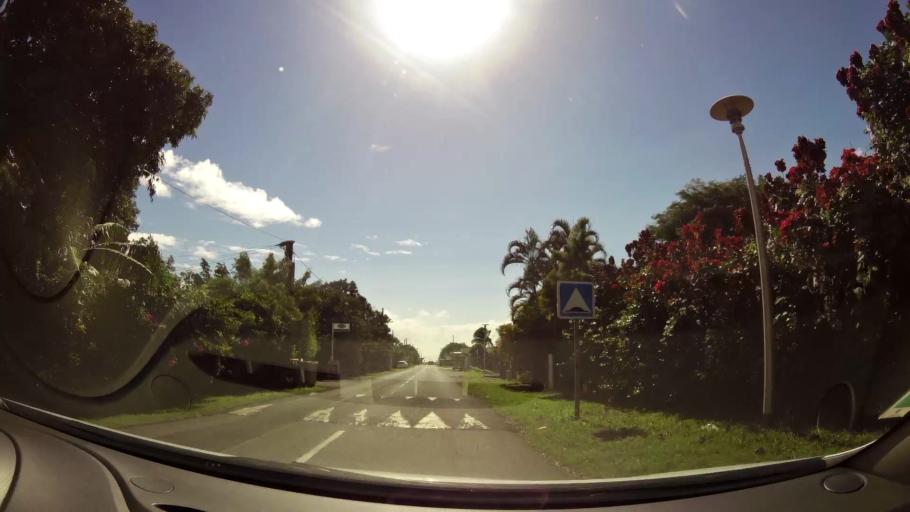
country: RE
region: Reunion
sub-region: Reunion
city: Sainte-Marie
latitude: -20.8943
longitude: 55.5093
